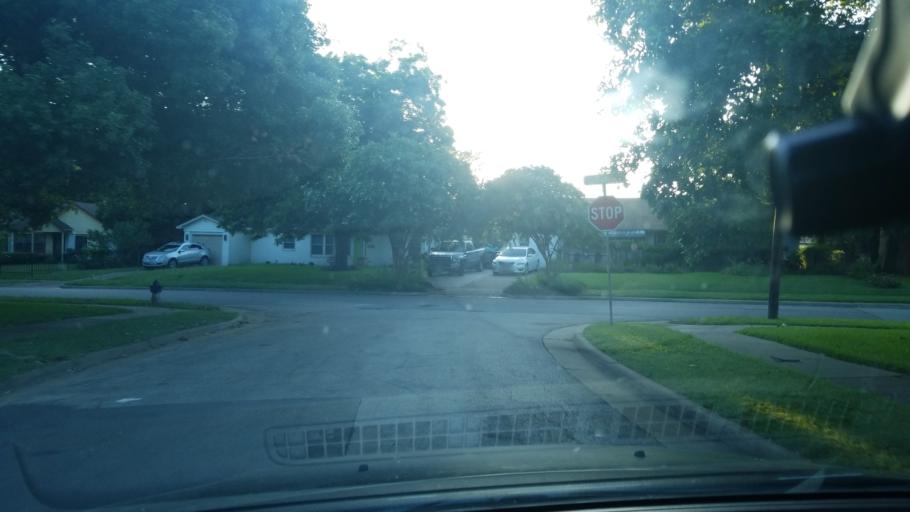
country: US
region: Texas
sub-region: Dallas County
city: Cockrell Hill
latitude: 32.7152
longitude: -96.8313
